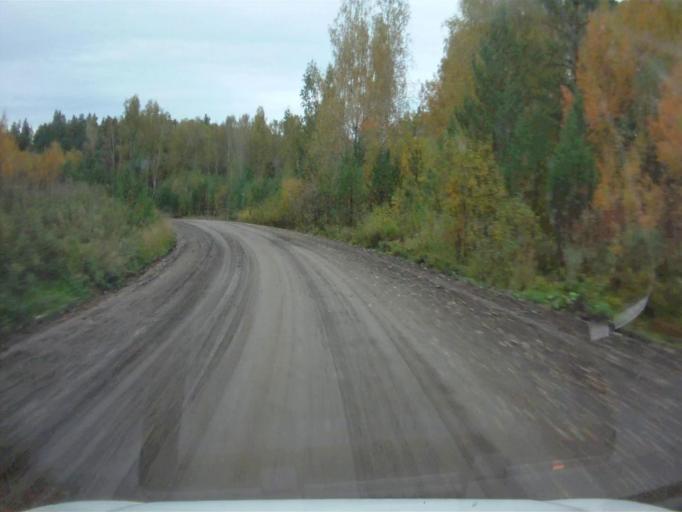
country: RU
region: Chelyabinsk
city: Nyazepetrovsk
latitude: 56.1202
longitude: 59.3697
